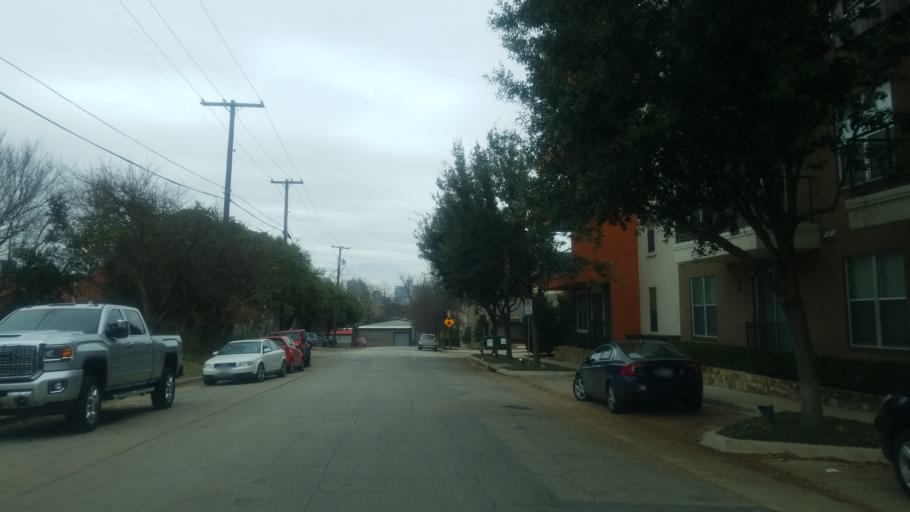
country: US
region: Texas
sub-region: Dallas County
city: Dallas
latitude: 32.8114
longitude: -96.8305
